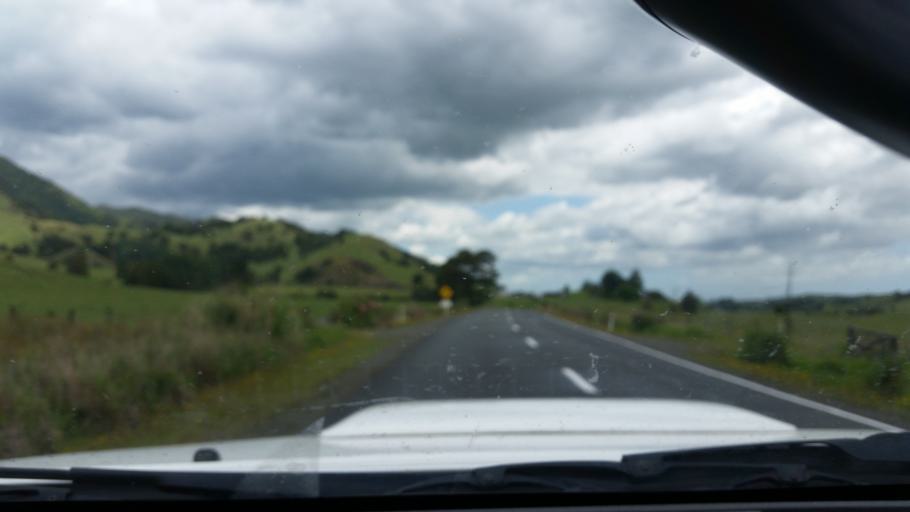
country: NZ
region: Northland
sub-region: Kaipara District
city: Dargaville
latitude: -35.7953
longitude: 173.9172
